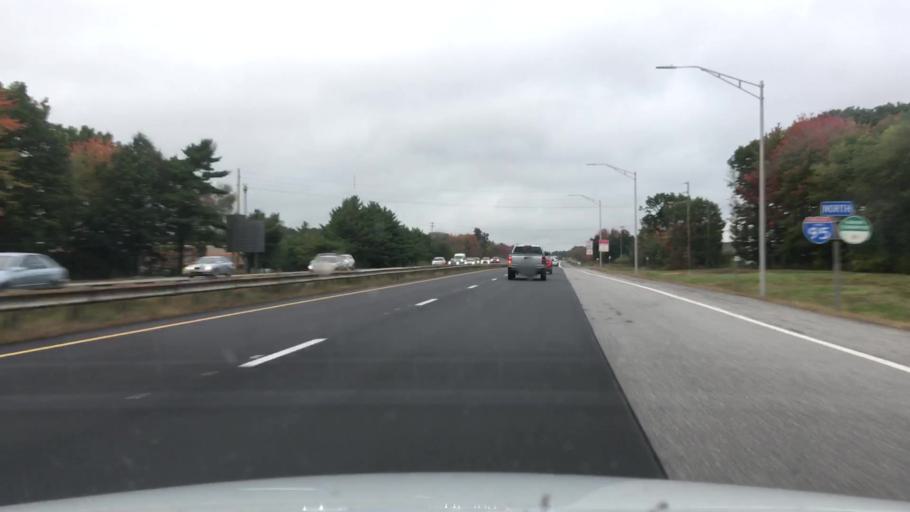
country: US
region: Maine
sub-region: Cumberland County
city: South Portland Gardens
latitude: 43.6833
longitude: -70.3238
